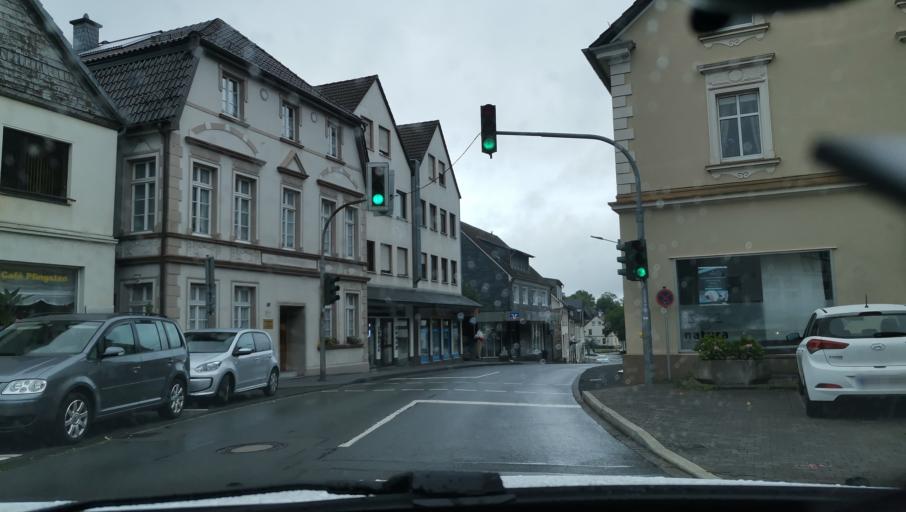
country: DE
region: North Rhine-Westphalia
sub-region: Regierungsbezirk Arnsberg
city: Breckerfeld
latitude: 51.2600
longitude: 7.4666
